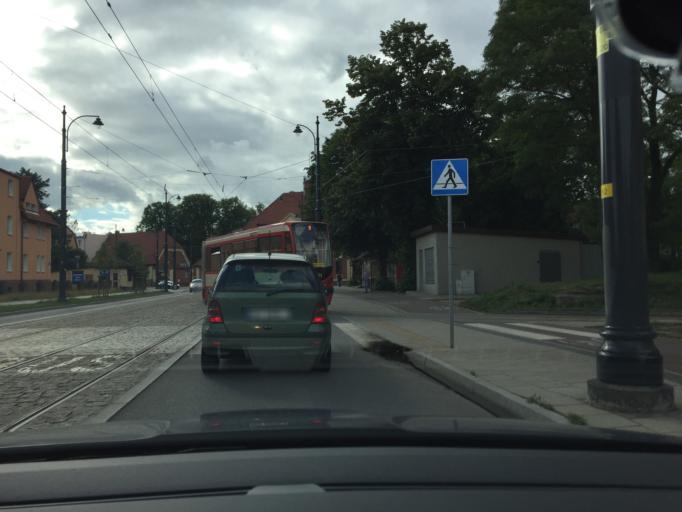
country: PL
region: Pomeranian Voivodeship
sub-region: Gdansk
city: Gdansk
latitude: 54.3574
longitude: 18.6843
